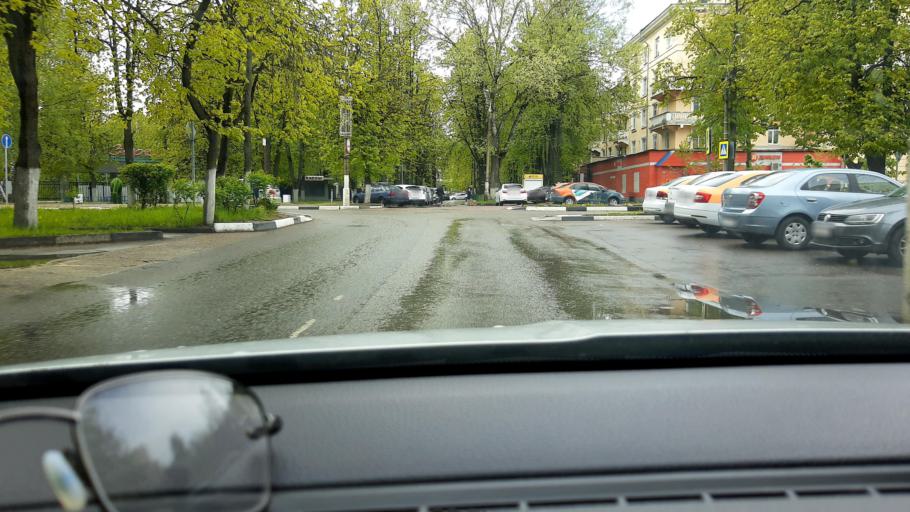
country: RU
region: Moskovskaya
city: Krasnogorsk
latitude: 55.8273
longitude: 37.3302
